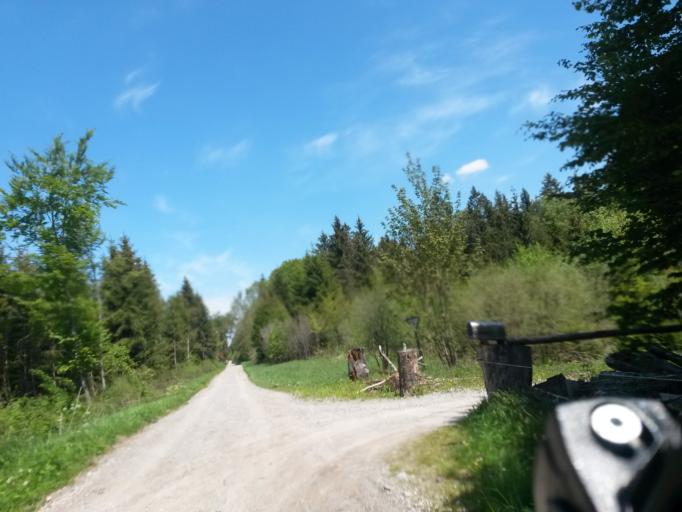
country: DE
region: Baden-Wuerttemberg
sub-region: Tuebingen Region
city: Bad Waldsee
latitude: 47.9352
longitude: 9.7028
